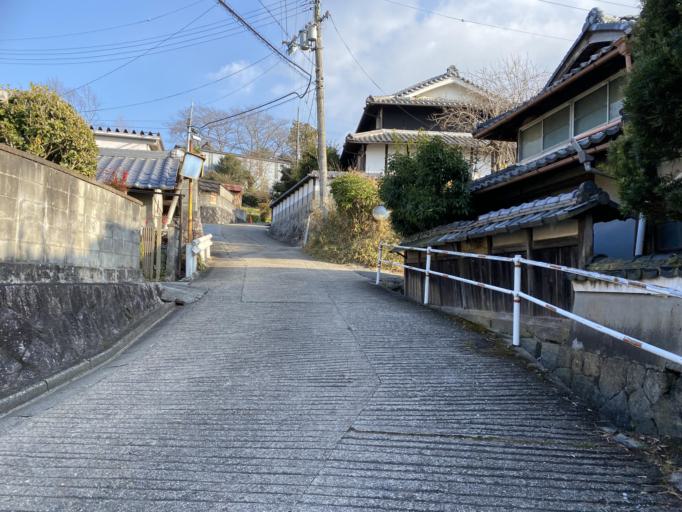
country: JP
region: Nara
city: Nara-shi
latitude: 34.7574
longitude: 135.8763
